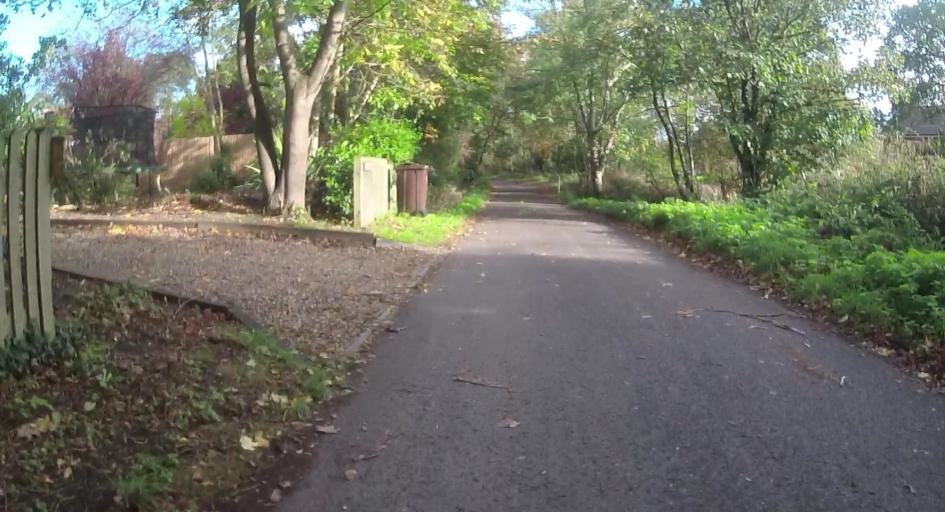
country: GB
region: England
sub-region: Wokingham
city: Swallowfield
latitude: 51.3960
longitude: -0.9605
